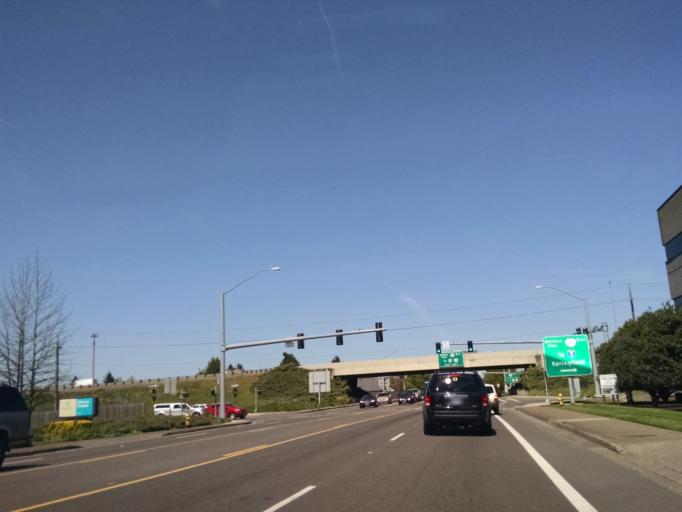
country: US
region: Oregon
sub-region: Lane County
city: Eugene
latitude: 44.0864
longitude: -123.0676
